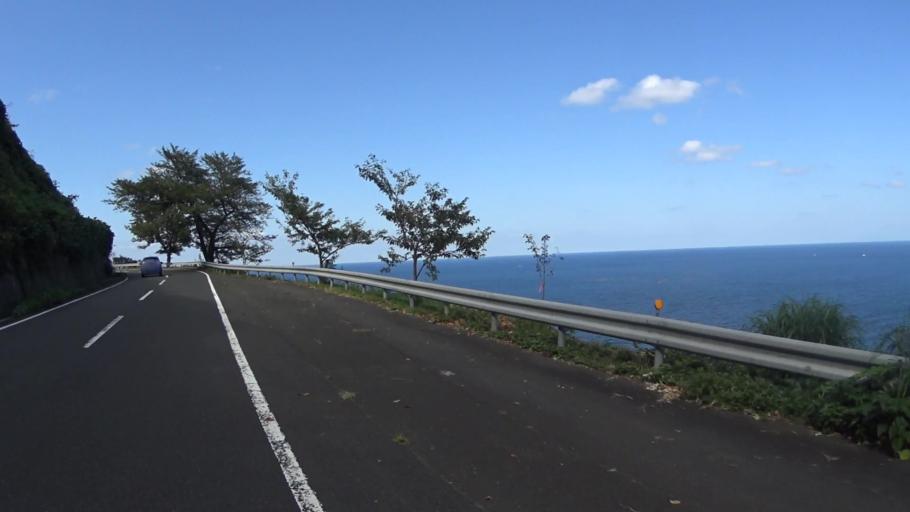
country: JP
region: Kyoto
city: Miyazu
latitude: 35.7579
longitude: 135.2450
